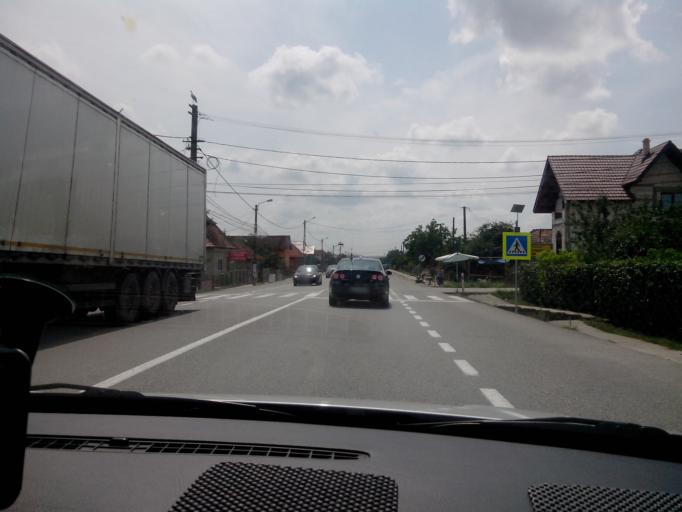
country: RO
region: Cluj
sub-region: Comuna Bontida
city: Rascruci
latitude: 46.9014
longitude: 23.7744
